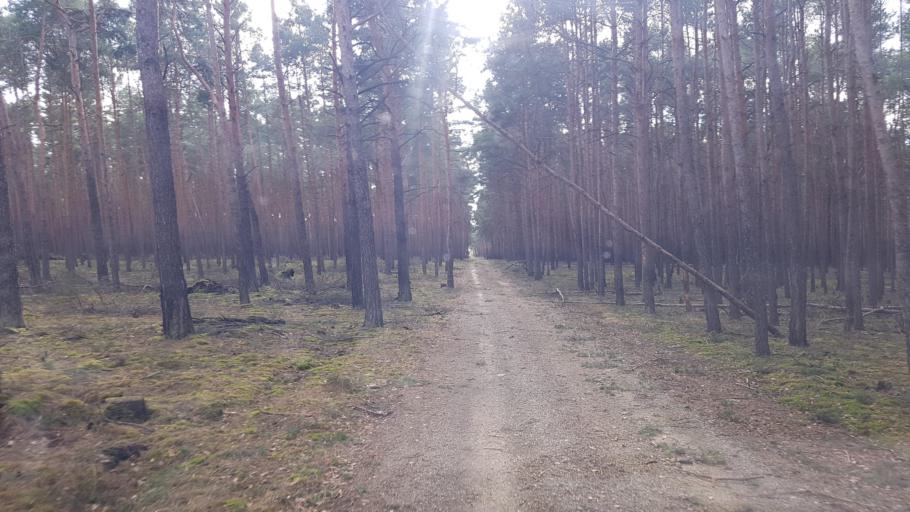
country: DE
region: Brandenburg
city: Schlieben
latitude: 51.6790
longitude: 13.4000
